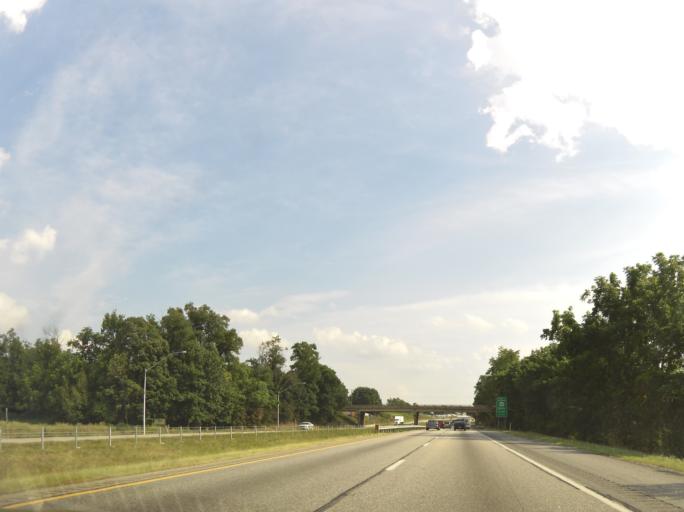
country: US
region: Pennsylvania
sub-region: Franklin County
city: State Line
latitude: 39.7336
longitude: -77.7270
